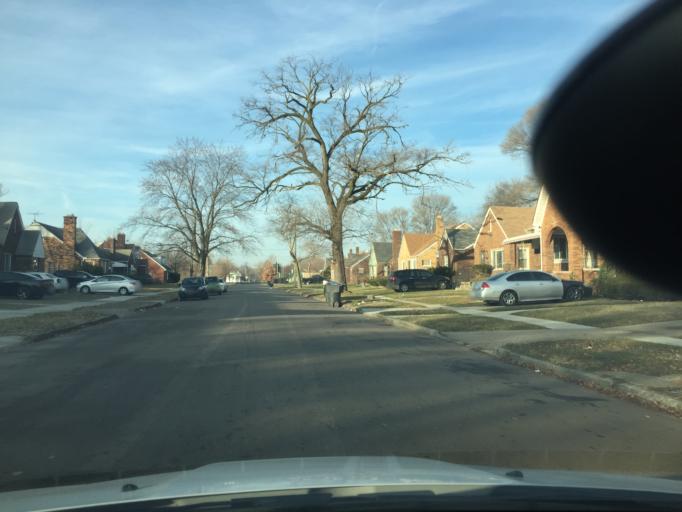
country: US
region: Michigan
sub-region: Macomb County
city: Eastpointe
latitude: 42.4417
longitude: -82.9701
